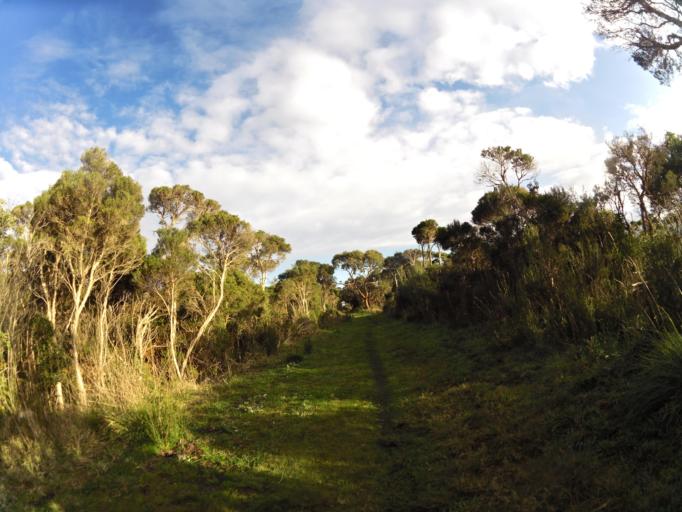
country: AU
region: Victoria
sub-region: Bass Coast
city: North Wonthaggi
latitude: -38.6011
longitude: 145.5641
